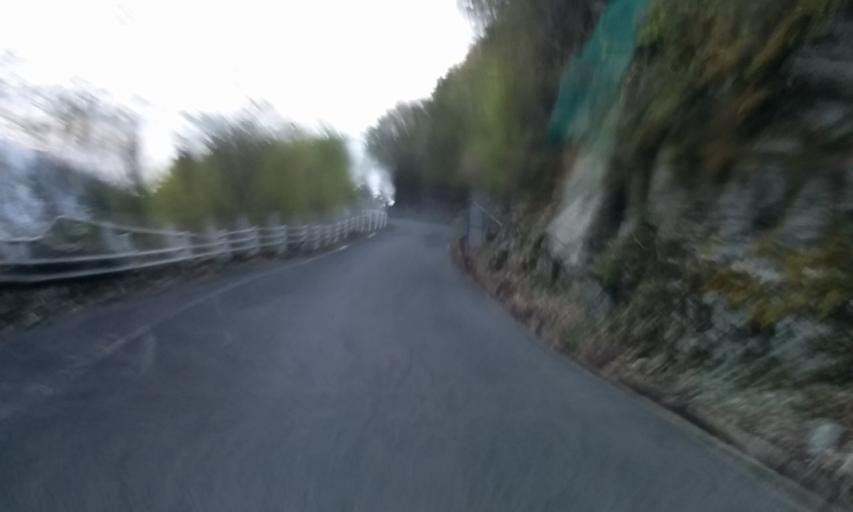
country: JP
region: Ehime
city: Saijo
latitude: 33.7912
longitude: 133.2784
